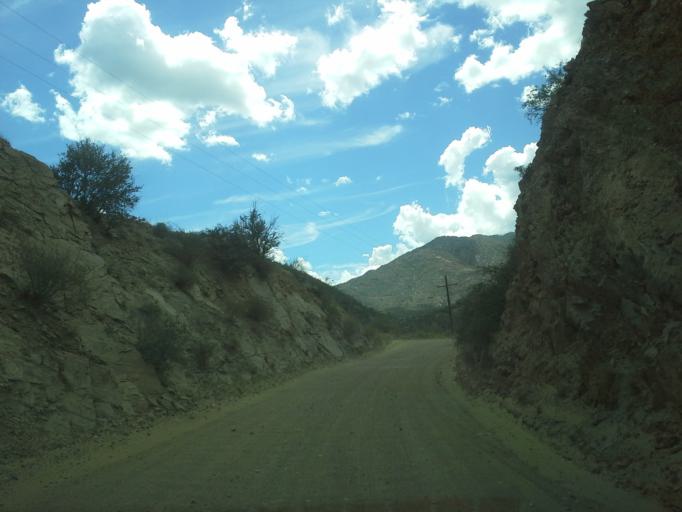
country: US
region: Arizona
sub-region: Yavapai County
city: Mayer
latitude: 34.2717
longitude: -112.2799
